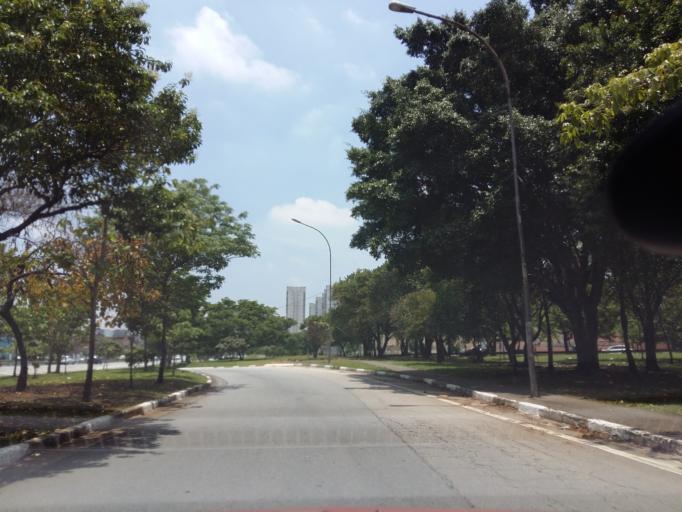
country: BR
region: Sao Paulo
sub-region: Diadema
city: Diadema
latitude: -23.6303
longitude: -46.6304
